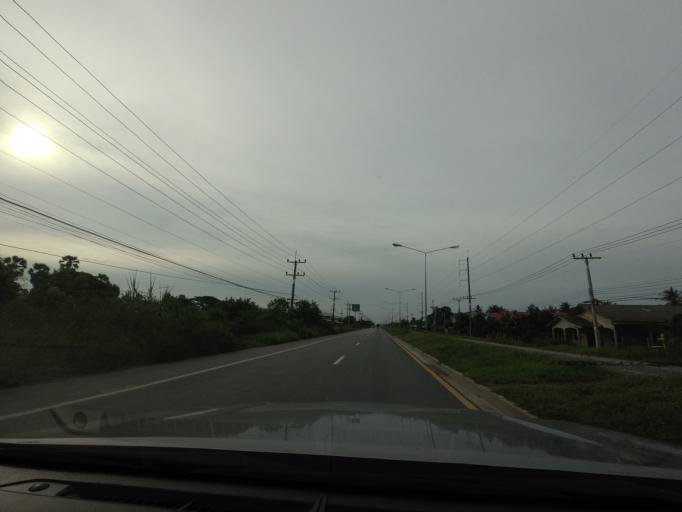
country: TH
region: Songkhla
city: Ranot
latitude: 7.7616
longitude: 100.3587
